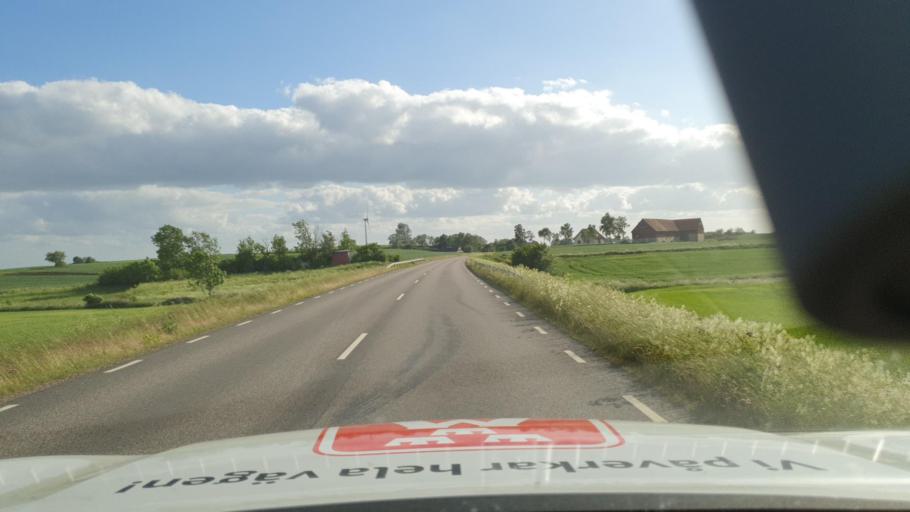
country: SE
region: Skane
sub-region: Tomelilla Kommun
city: Tomelilla
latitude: 55.5737
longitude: 13.9976
